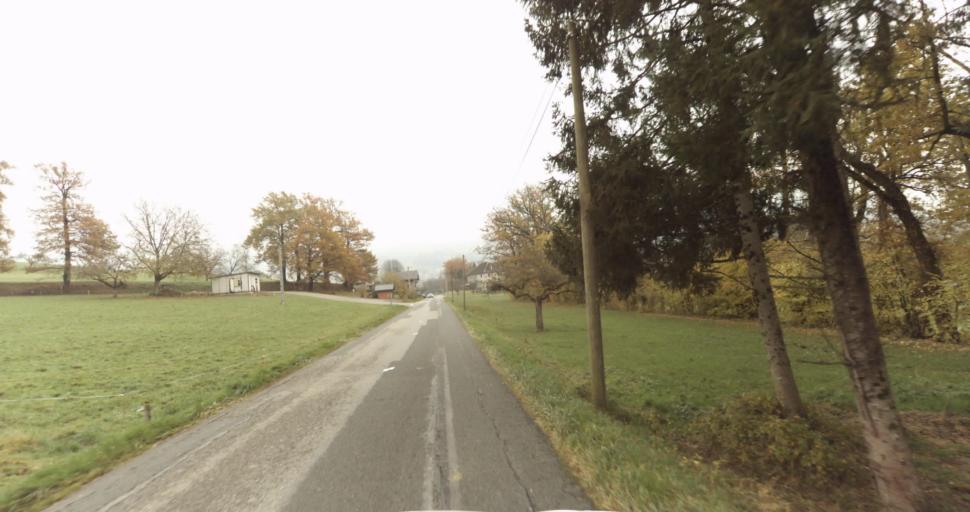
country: FR
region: Rhone-Alpes
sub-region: Departement de la Haute-Savoie
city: Gruffy
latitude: 45.7943
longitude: 6.0385
